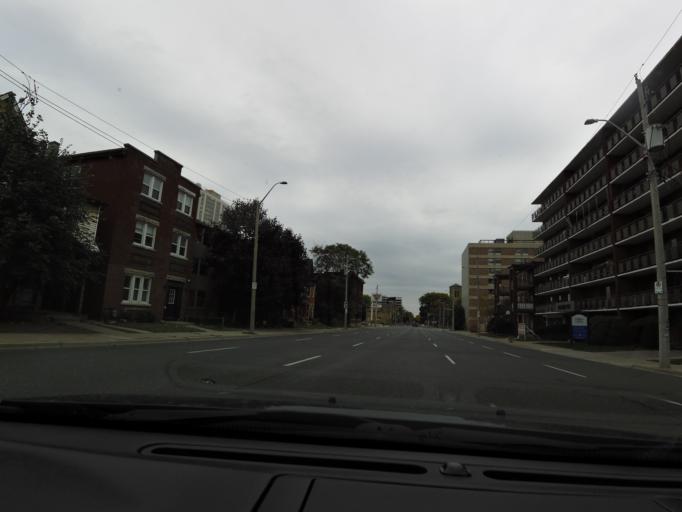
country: CA
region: Ontario
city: Hamilton
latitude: 43.2510
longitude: -79.8578
